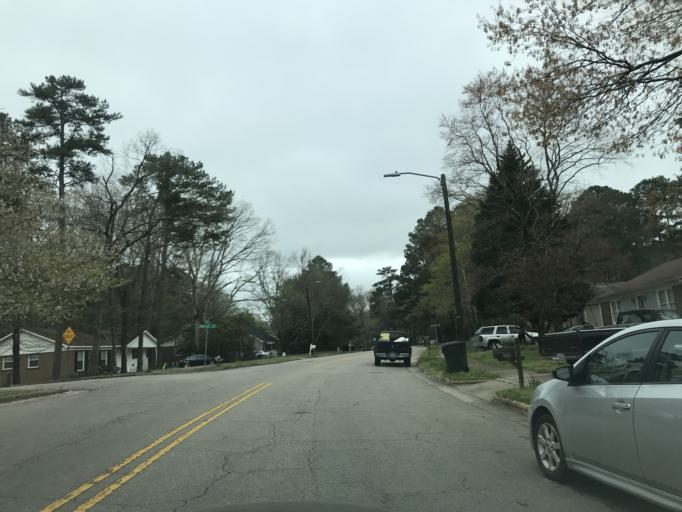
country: US
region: North Carolina
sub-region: Wake County
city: West Raleigh
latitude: 35.8806
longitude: -78.6488
